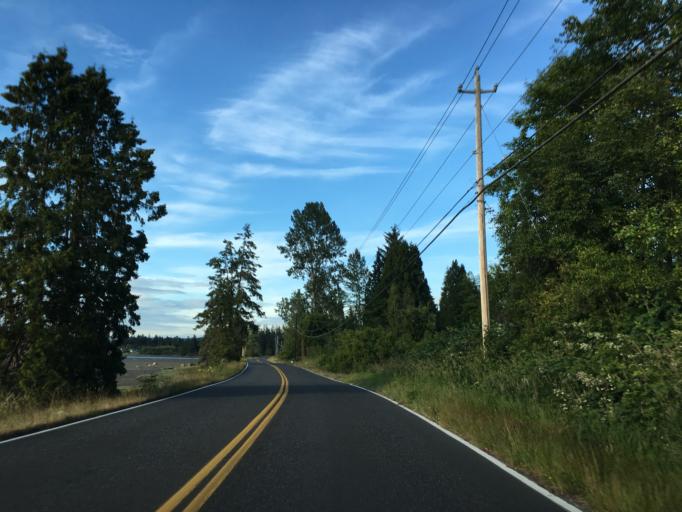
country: US
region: Washington
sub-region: Whatcom County
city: Blaine
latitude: 48.9589
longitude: -122.7435
